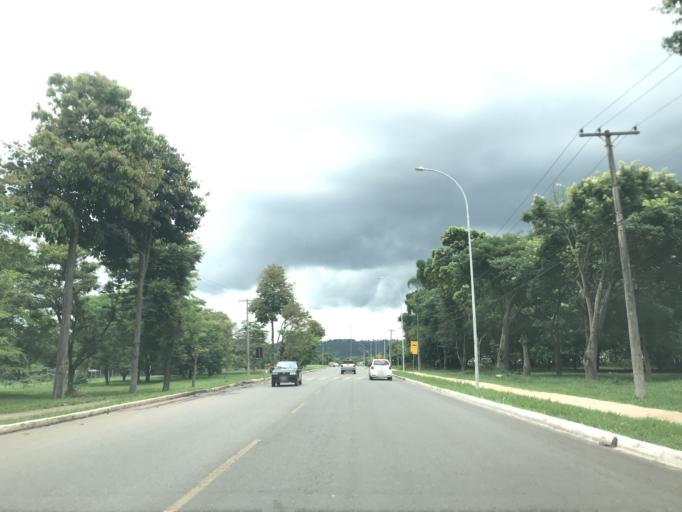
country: BR
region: Federal District
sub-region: Brasilia
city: Brasilia
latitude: -15.6521
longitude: -47.8137
